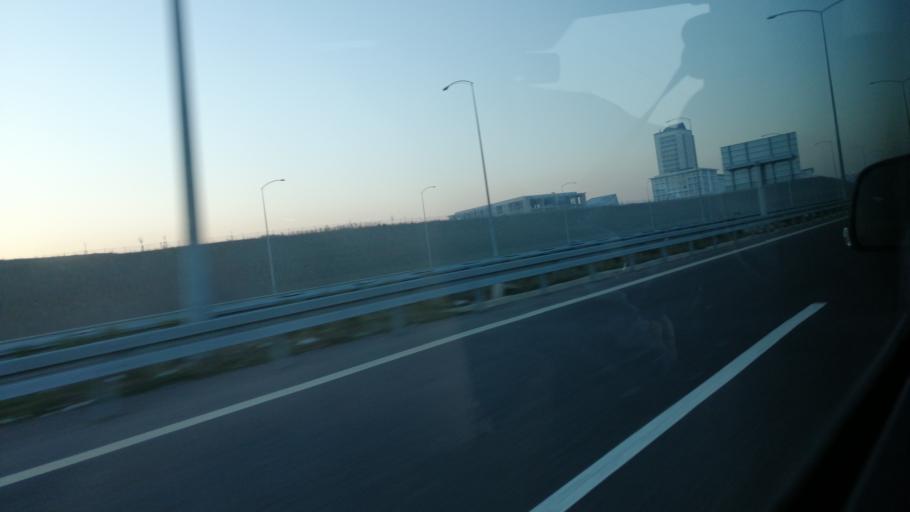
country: TR
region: Kocaeli
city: Tavsanli
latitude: 40.7872
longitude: 29.5152
